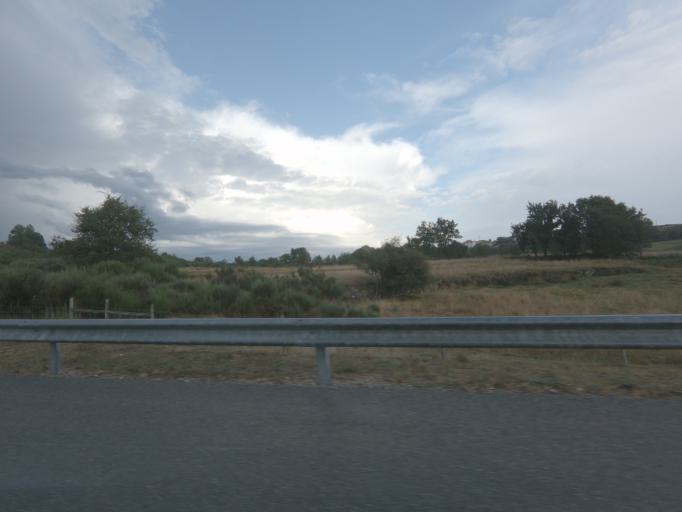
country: PT
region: Viseu
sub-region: Castro Daire
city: Castro Daire
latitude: 40.9628
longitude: -7.8903
